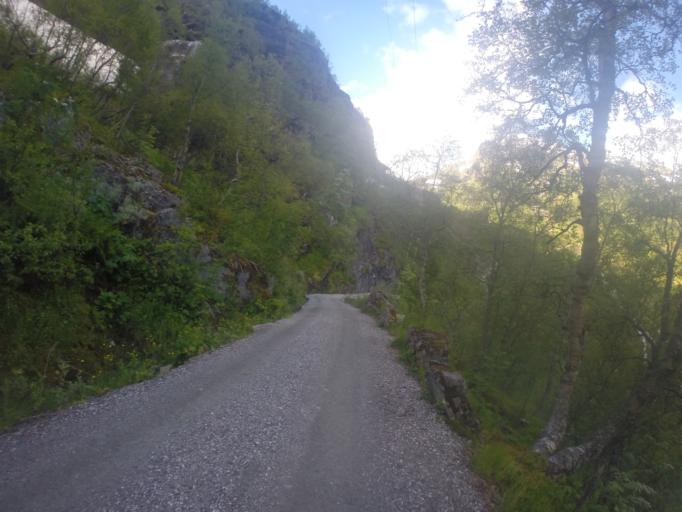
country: NO
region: Sogn og Fjordane
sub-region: Aurland
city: Aurlandsvangen
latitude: 60.7415
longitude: 7.1272
